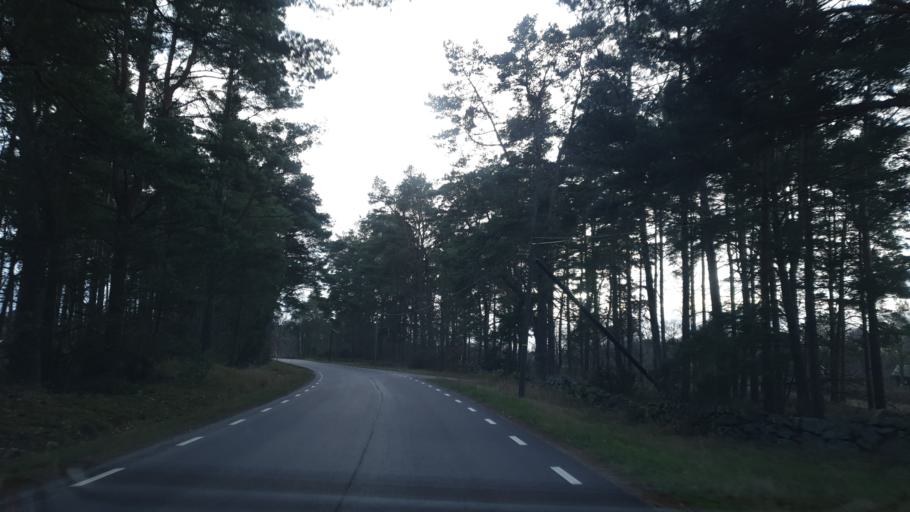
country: SE
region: Kalmar
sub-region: Torsas Kommun
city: Torsas
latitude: 56.2490
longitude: 16.0049
